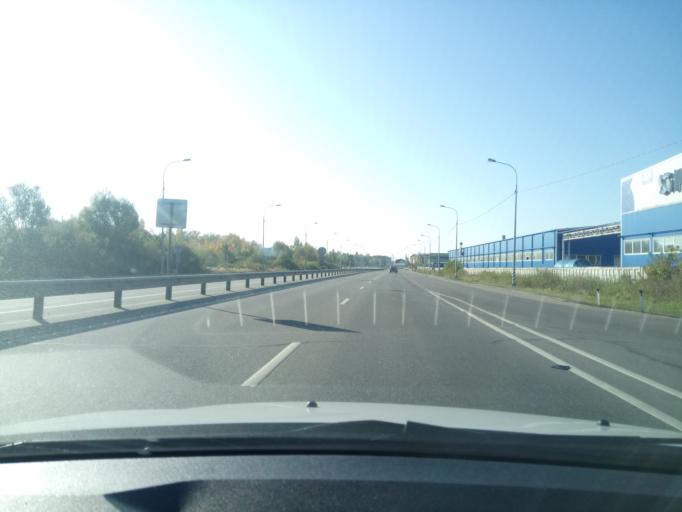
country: RU
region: Nizjnij Novgorod
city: Burevestnik
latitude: 56.1721
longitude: 43.9154
